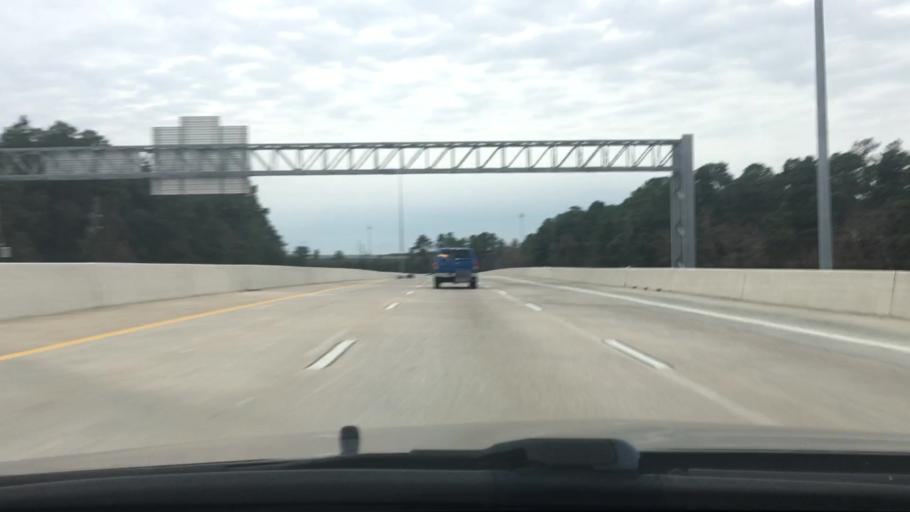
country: US
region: Texas
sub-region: Harris County
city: Spring
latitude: 30.0744
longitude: -95.4116
